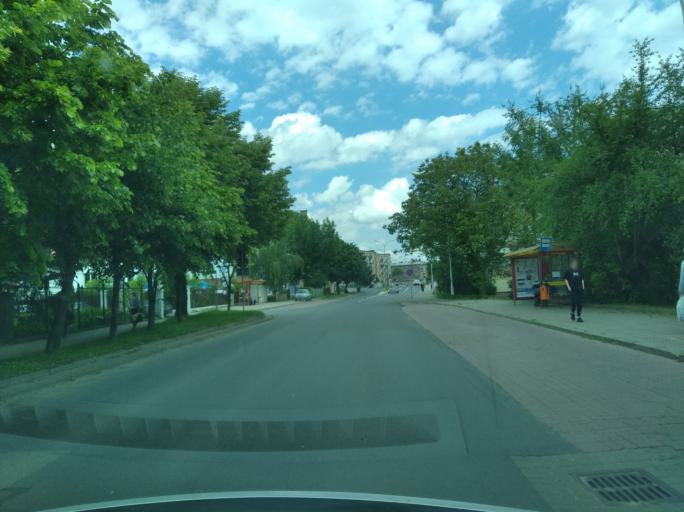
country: PL
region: Subcarpathian Voivodeship
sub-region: Przemysl
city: Przemysl
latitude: 49.7889
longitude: 22.7718
